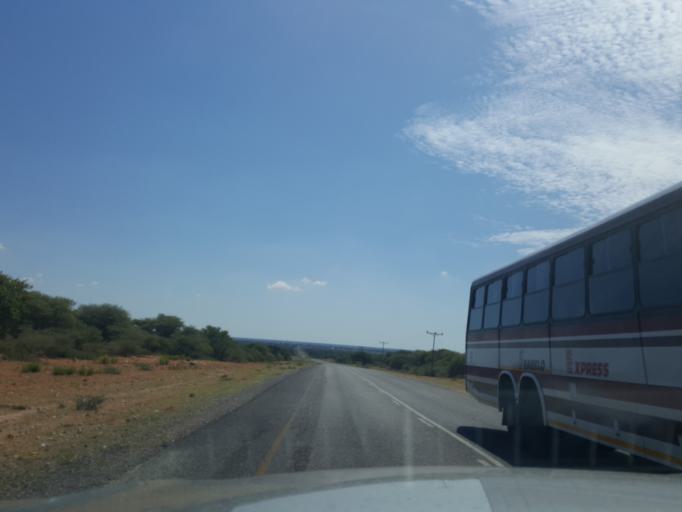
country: BW
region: Kweneng
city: Letlhakeng
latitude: -24.1219
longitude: 25.0854
